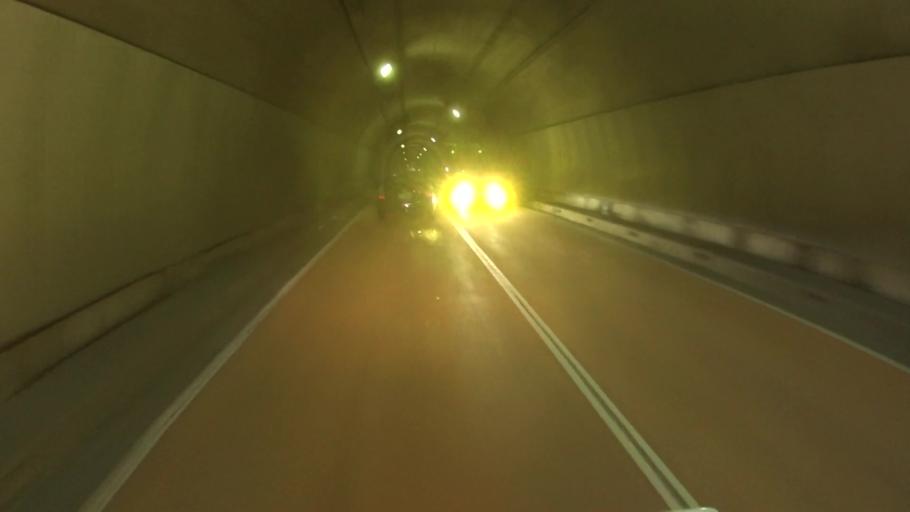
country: JP
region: Kyoto
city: Ayabe
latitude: 35.2728
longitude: 135.2661
